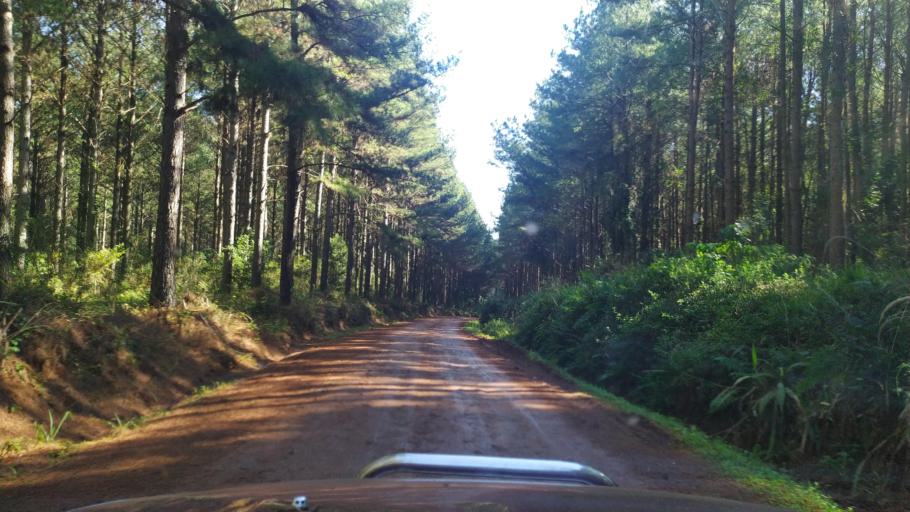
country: AR
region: Misiones
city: El Alcazar
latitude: -26.7359
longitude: -54.6511
